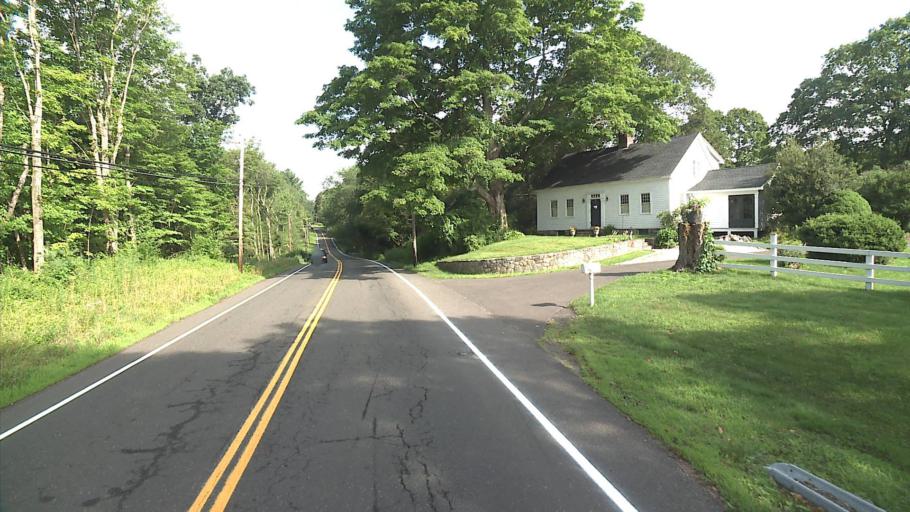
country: US
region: Connecticut
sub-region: New Haven County
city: Woodbridge
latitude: 41.3550
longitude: -73.0365
